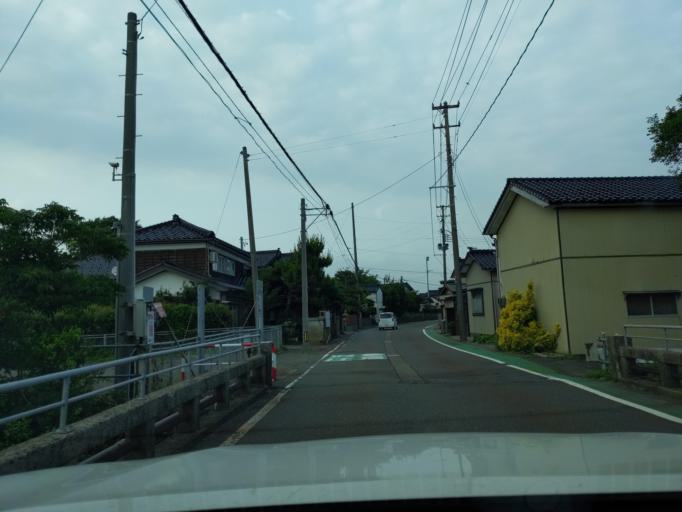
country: JP
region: Niigata
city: Kashiwazaki
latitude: 37.3834
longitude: 138.5741
